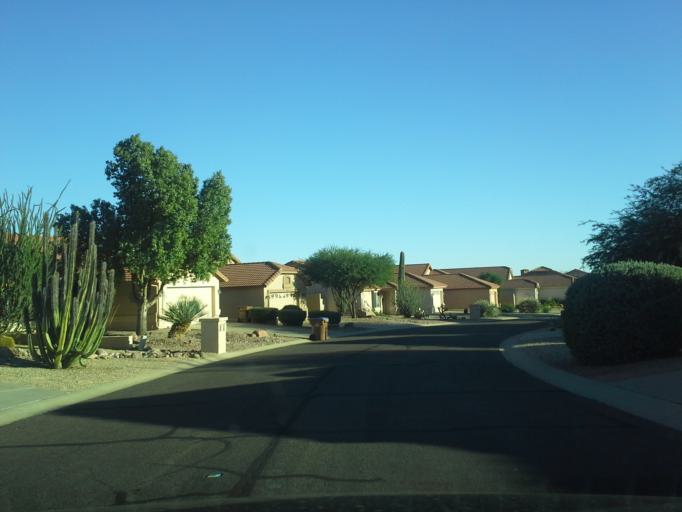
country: US
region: Arizona
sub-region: Pinal County
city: Apache Junction
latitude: 33.3724
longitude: -111.4346
